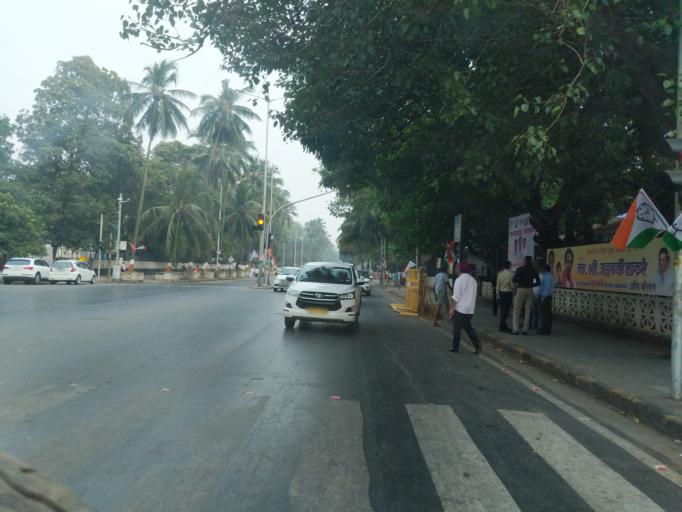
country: IN
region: Maharashtra
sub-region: Raigarh
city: Uran
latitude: 18.9289
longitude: 72.8230
